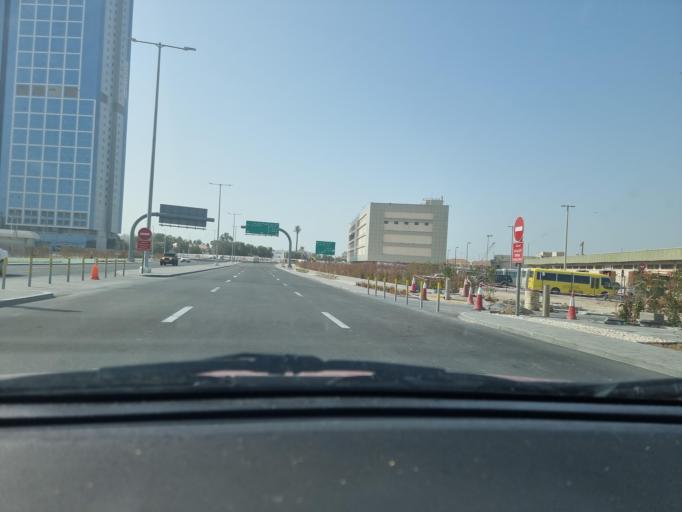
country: AE
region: Abu Dhabi
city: Abu Dhabi
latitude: 24.5088
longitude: 54.3800
